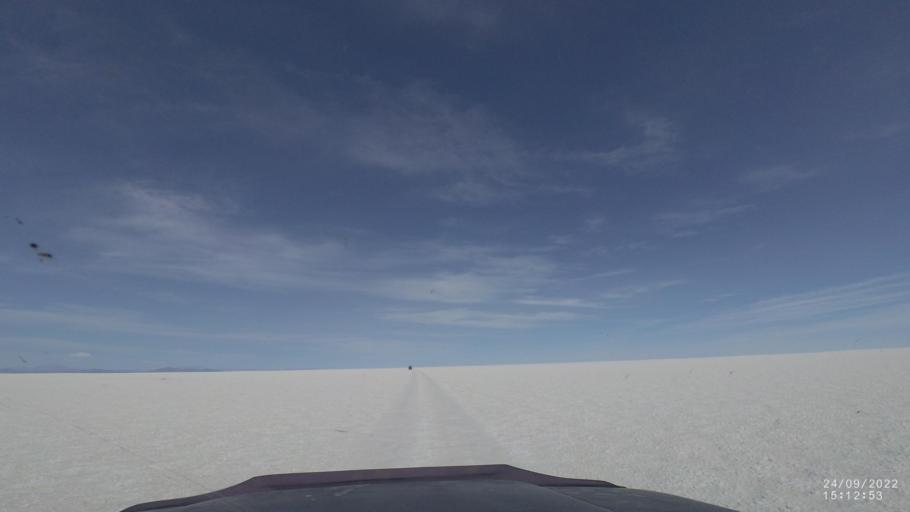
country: BO
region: Potosi
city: Colchani
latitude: -19.9529
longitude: -67.4683
